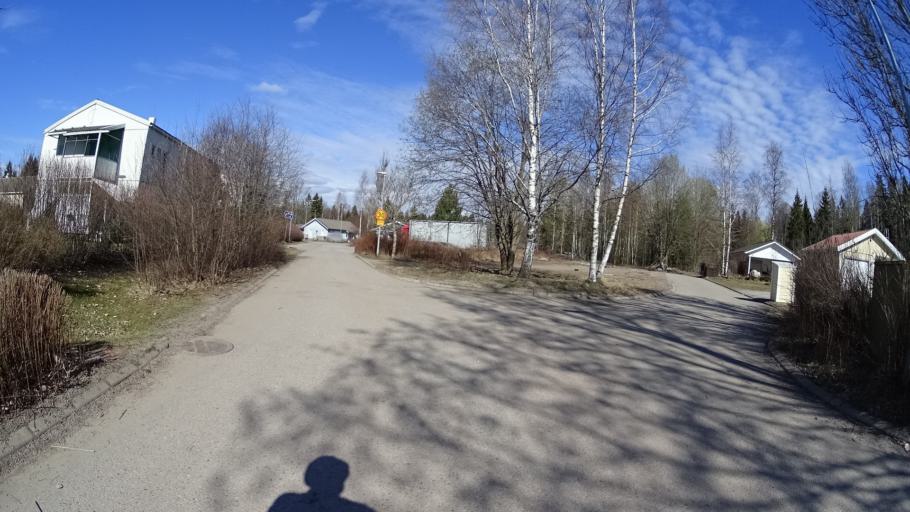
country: FI
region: Uusimaa
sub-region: Helsinki
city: Kilo
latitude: 60.2831
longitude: 24.7548
